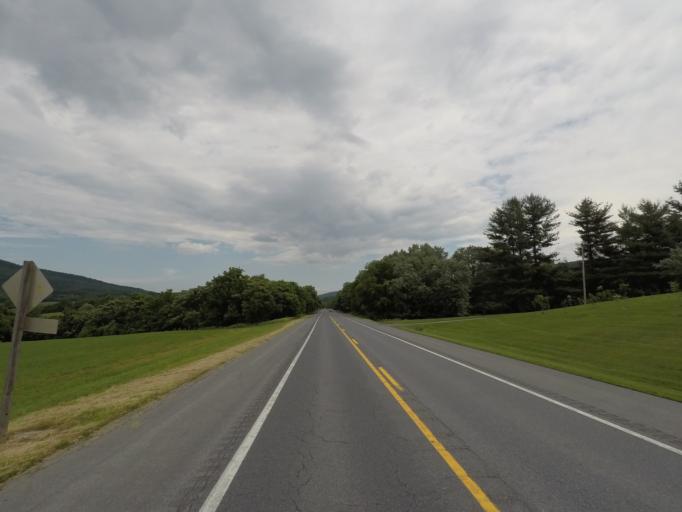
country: US
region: Maryland
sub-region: Frederick County
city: Brunswick
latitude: 39.3686
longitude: -77.6706
